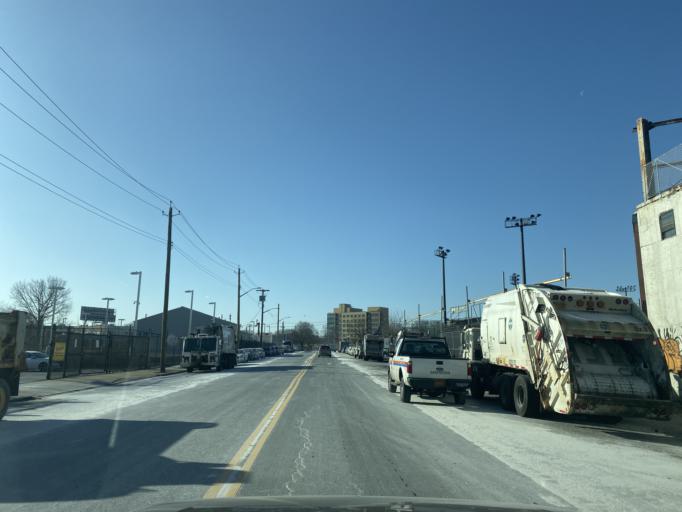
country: US
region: New York
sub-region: Bronx
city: The Bronx
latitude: 40.8327
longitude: -73.8427
